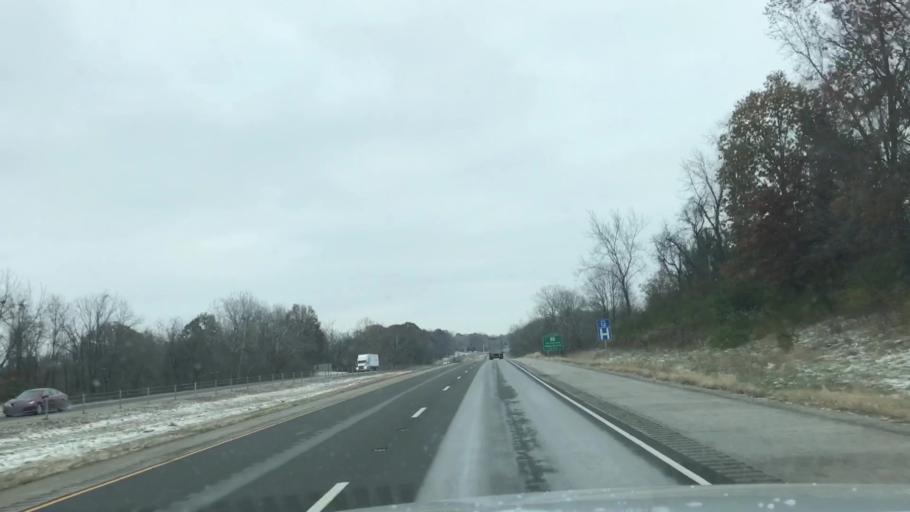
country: US
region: Illinois
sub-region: Madison County
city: Glen Carbon
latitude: 38.7569
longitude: -89.9710
